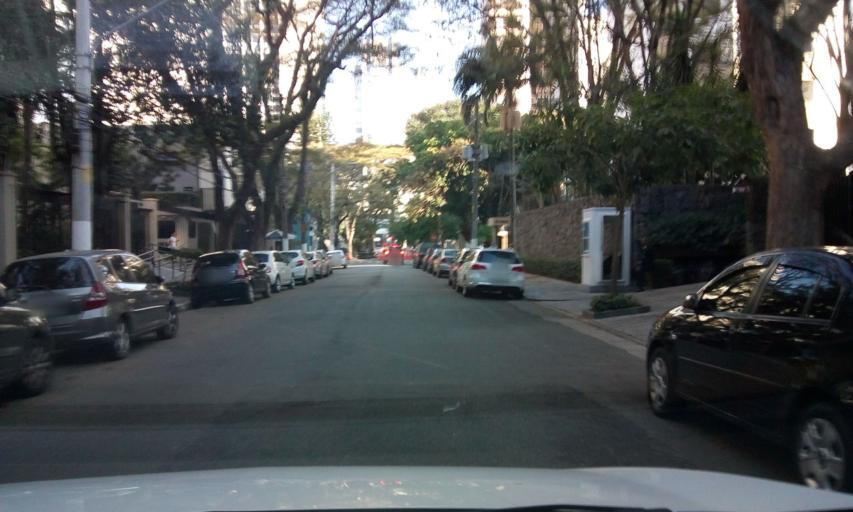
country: BR
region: Sao Paulo
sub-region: Sao Paulo
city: Sao Paulo
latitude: -23.5933
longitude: -46.6682
